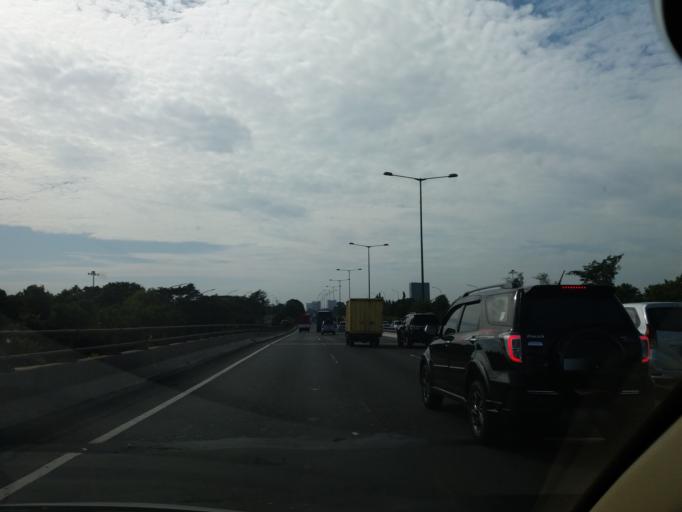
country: ID
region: Jakarta Raya
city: Jakarta
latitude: -6.2180
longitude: 106.8742
